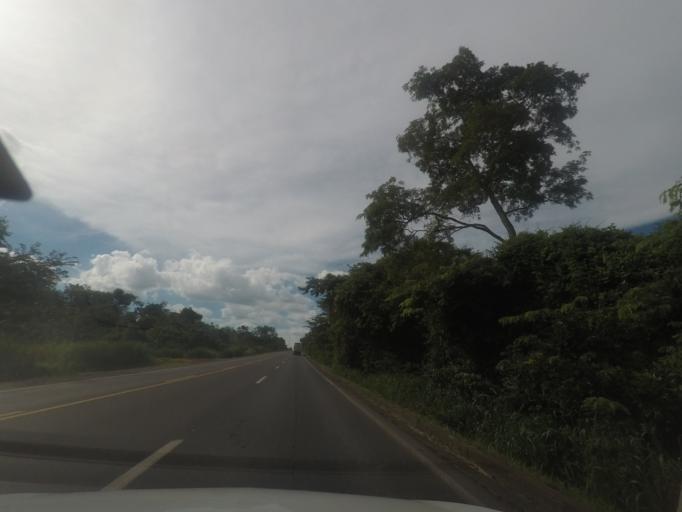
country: BR
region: Minas Gerais
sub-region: Prata
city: Prata
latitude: -19.1735
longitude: -48.9525
